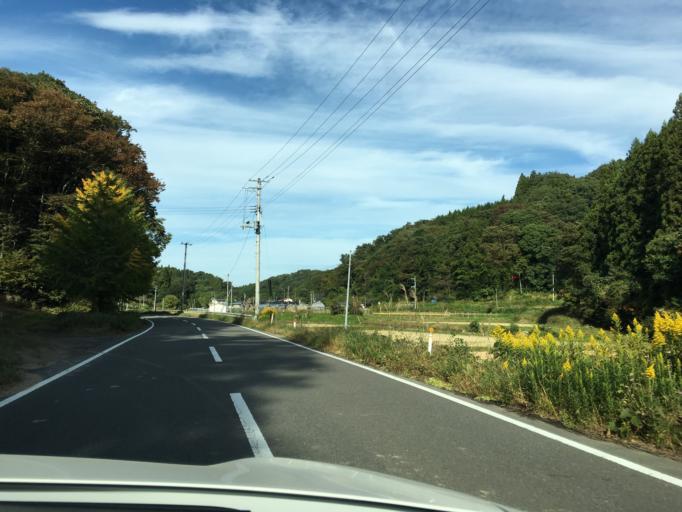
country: JP
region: Fukushima
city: Miharu
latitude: 37.3385
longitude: 140.5038
